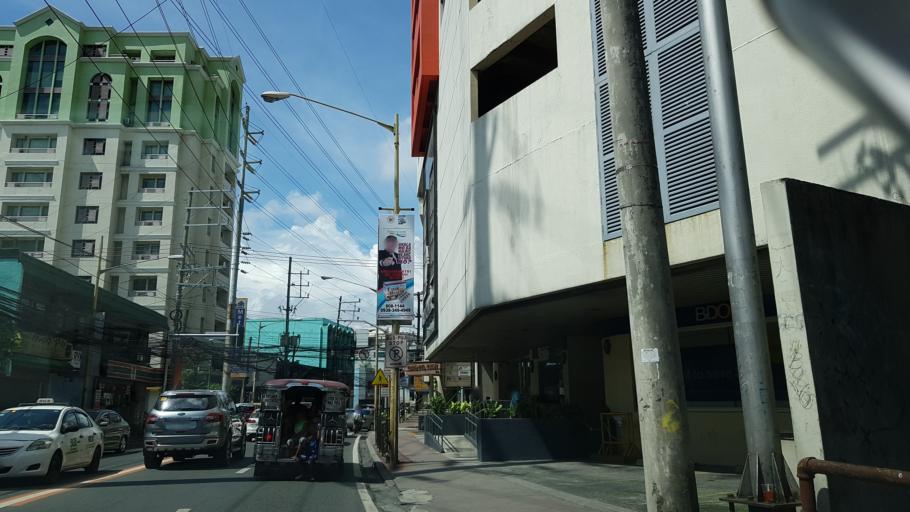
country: PH
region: Metro Manila
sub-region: Makati City
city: Makati City
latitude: 14.5614
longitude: 121.0110
